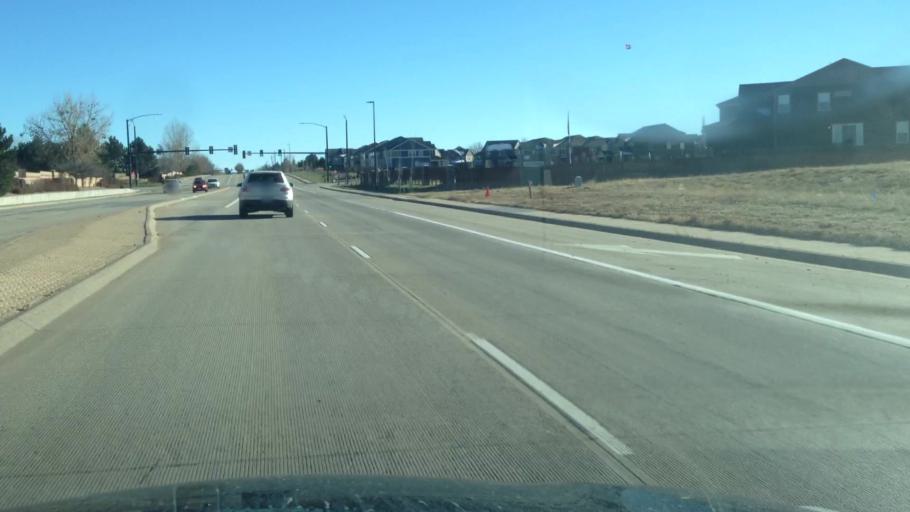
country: US
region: Colorado
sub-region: Arapahoe County
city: Dove Valley
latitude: 39.5694
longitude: -104.8039
